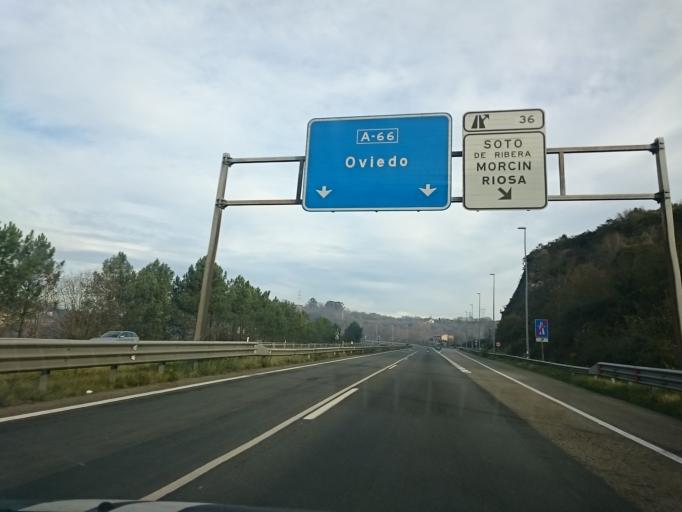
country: ES
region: Asturias
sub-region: Province of Asturias
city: Castandiello
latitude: 43.3154
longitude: -5.8677
